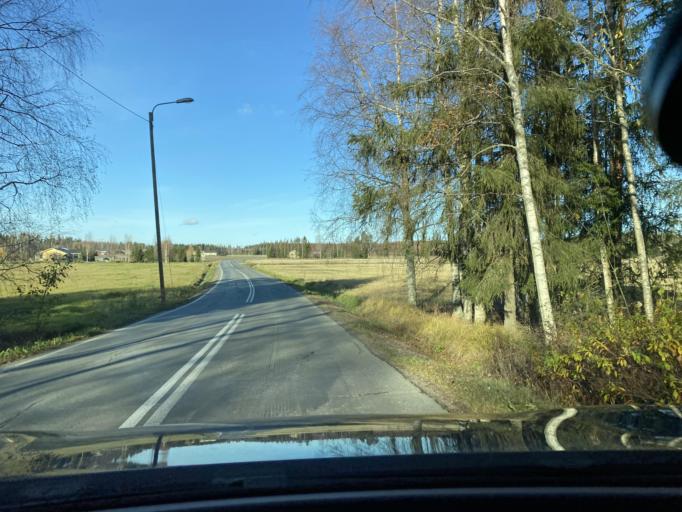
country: FI
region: Haeme
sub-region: Forssa
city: Tammela
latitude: 60.8300
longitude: 23.8409
